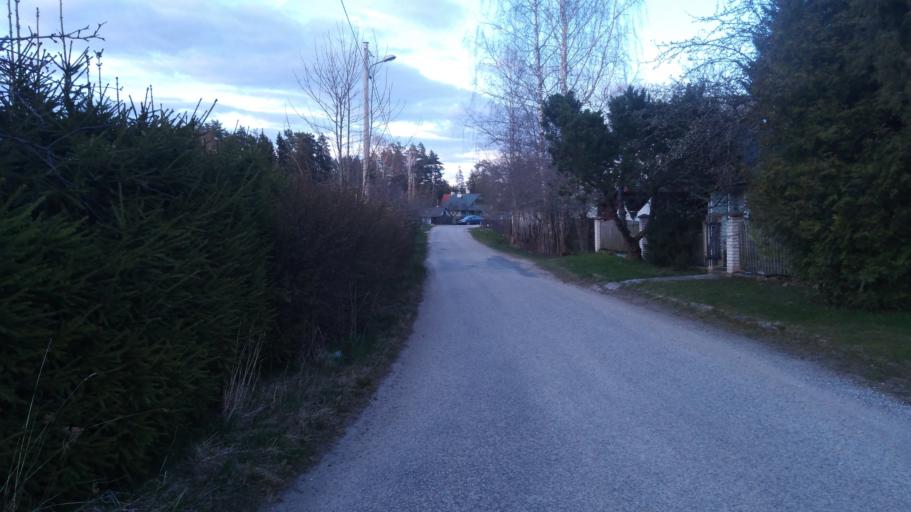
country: EE
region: Vorumaa
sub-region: Voru linn
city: Voru
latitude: 57.8070
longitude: 27.0120
